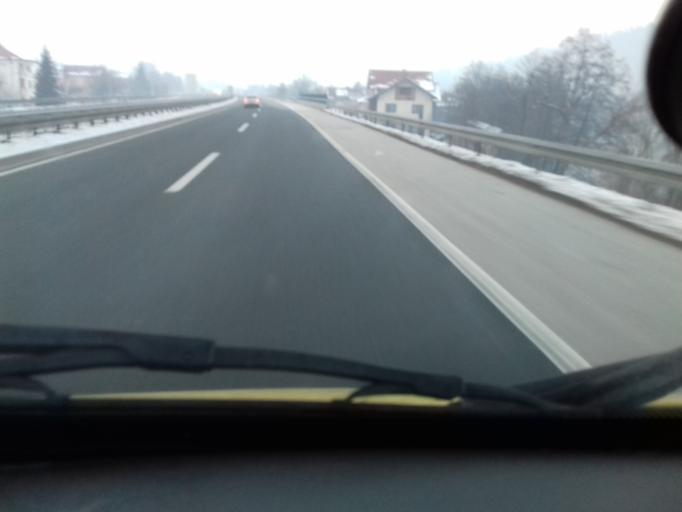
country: BA
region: Federation of Bosnia and Herzegovina
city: Vogosca
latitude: 43.9156
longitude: 18.3170
